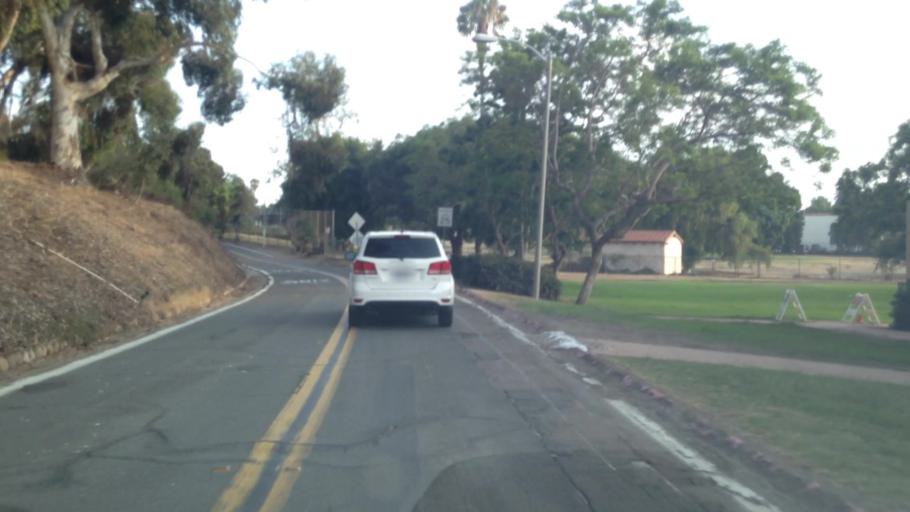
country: US
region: California
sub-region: San Diego County
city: San Diego
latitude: 32.7583
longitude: -117.1958
